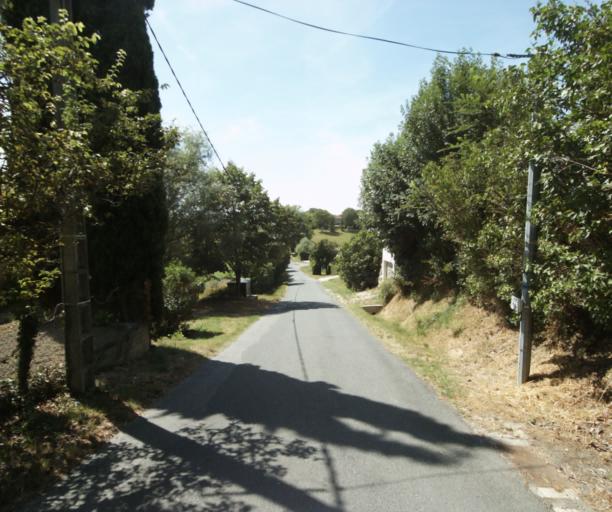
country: FR
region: Midi-Pyrenees
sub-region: Departement du Tarn
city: Puylaurens
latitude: 43.5271
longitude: 2.0077
